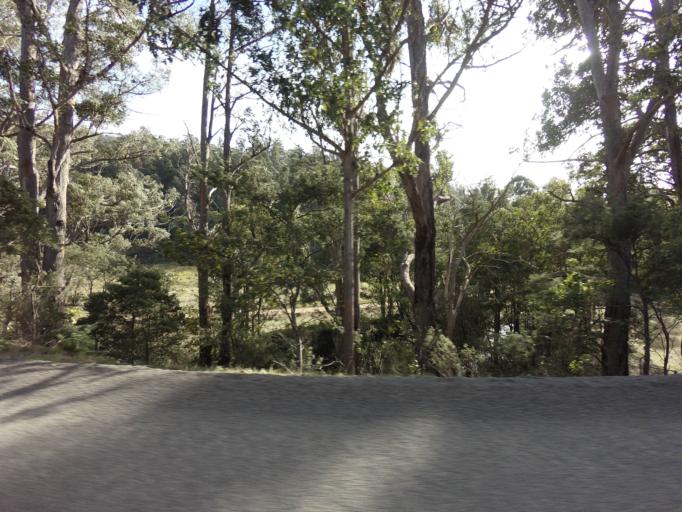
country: AU
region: Tasmania
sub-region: Huon Valley
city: Huonville
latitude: -43.0442
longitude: 147.1181
